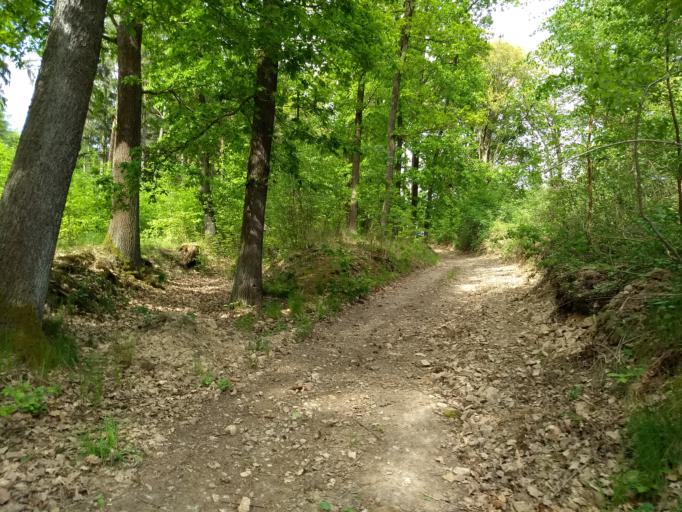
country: CZ
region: Central Bohemia
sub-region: Okres Beroun
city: Lodenice
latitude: 50.0445
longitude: 14.1606
